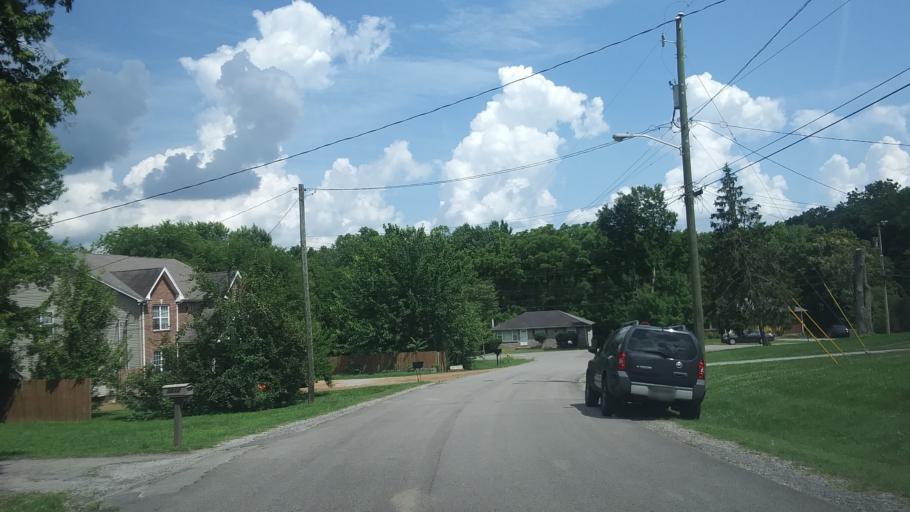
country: US
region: Tennessee
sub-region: Davidson County
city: Oak Hill
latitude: 36.0710
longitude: -86.7050
